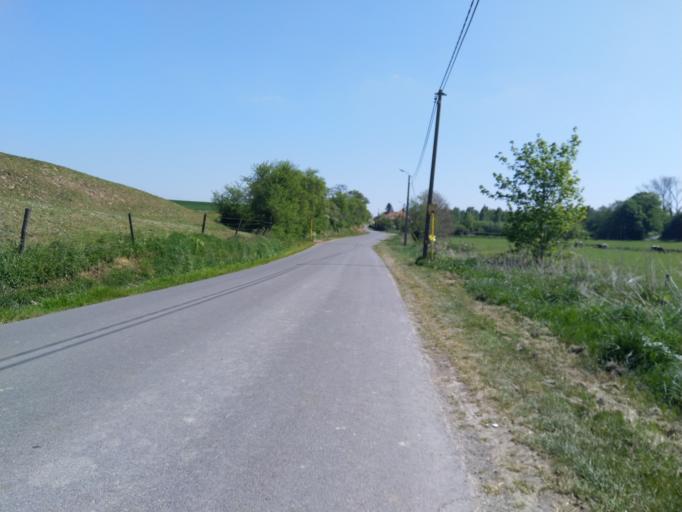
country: BE
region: Wallonia
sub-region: Province du Brabant Wallon
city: Rebecq-Rognon
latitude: 50.6182
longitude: 4.1055
